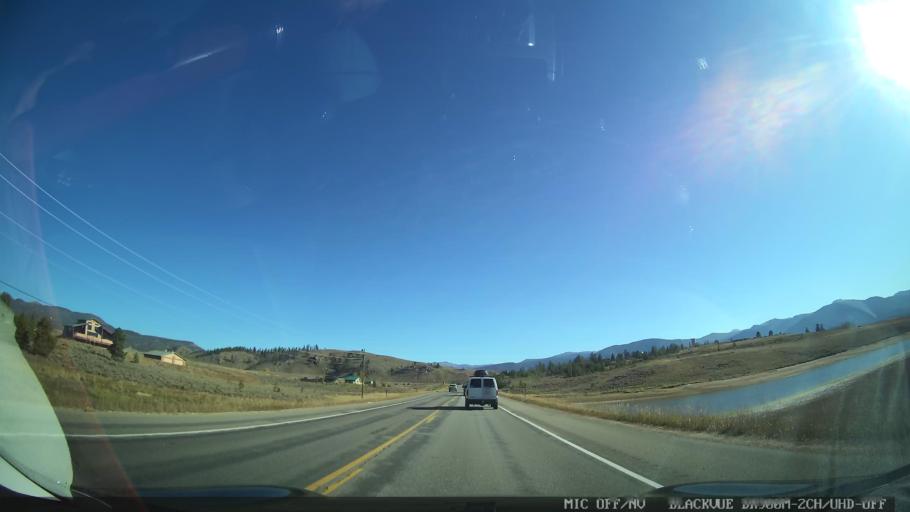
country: US
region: Colorado
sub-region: Grand County
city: Granby
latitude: 40.1783
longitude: -105.8951
